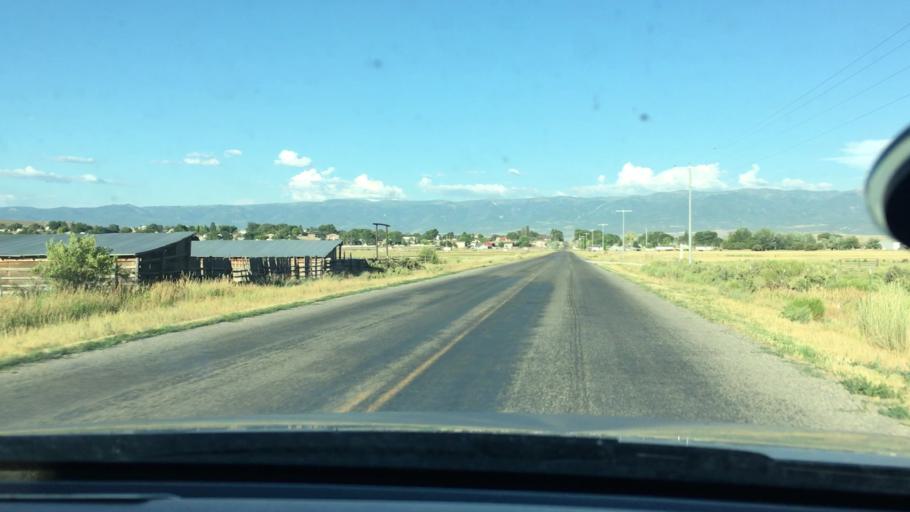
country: US
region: Utah
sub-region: Sanpete County
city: Moroni
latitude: 39.5235
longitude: -111.6028
